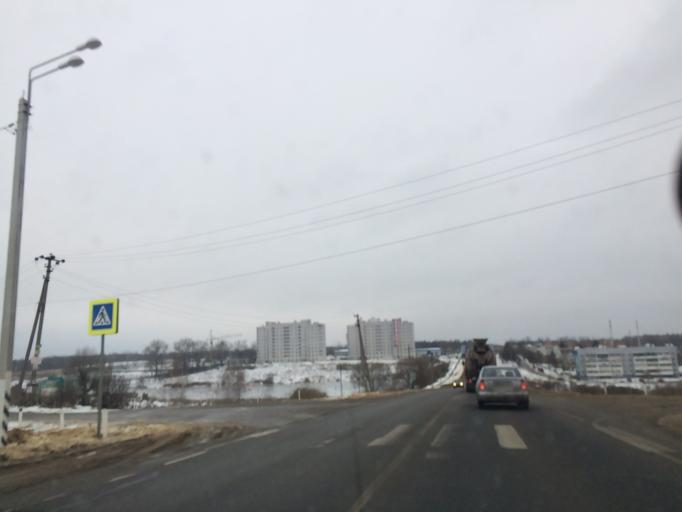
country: RU
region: Tula
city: Kosaya Gora
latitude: 54.1604
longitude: 37.4767
